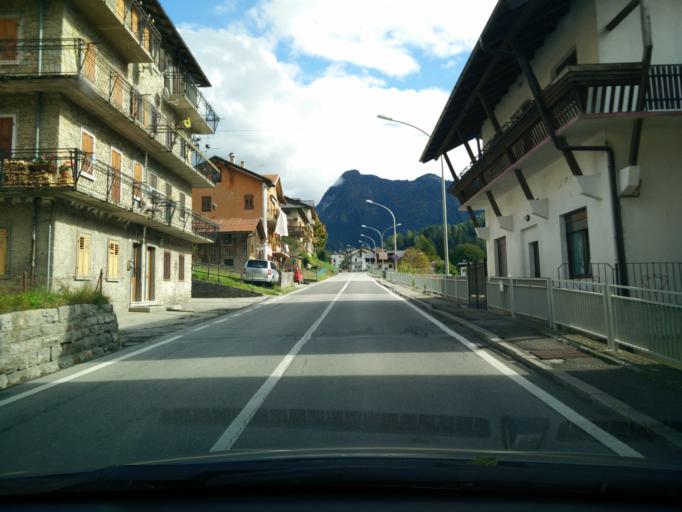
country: IT
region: Veneto
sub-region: Provincia di Belluno
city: Lorenzago di Cadore
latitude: 46.4901
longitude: 12.4572
